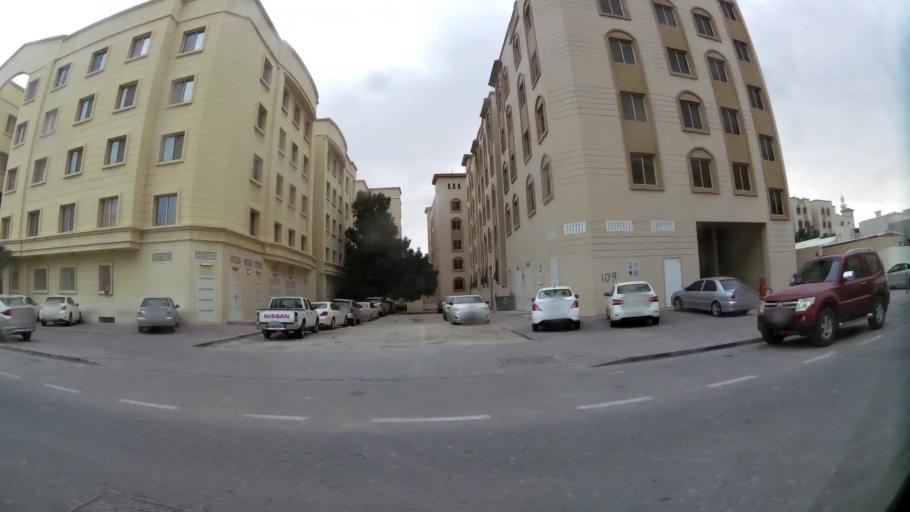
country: QA
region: Baladiyat ad Dawhah
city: Doha
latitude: 25.2773
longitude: 51.5011
